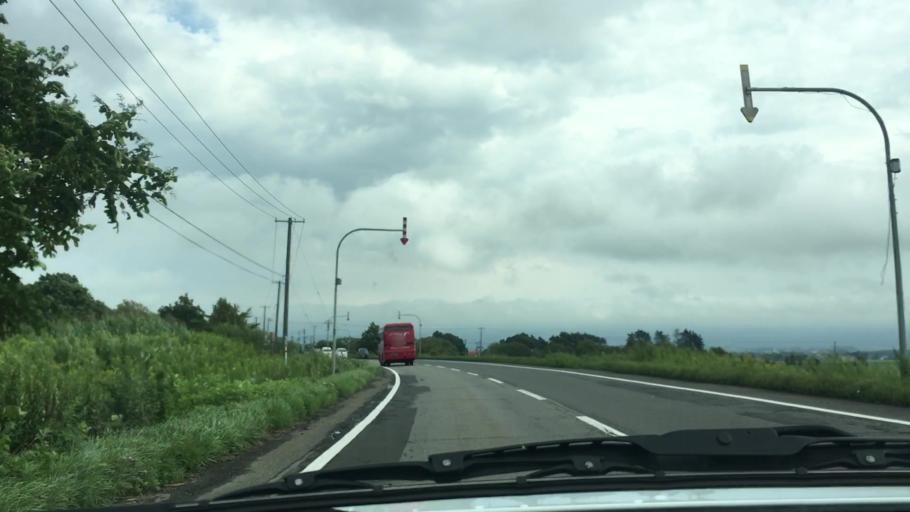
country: JP
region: Hokkaido
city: Chitose
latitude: 42.9431
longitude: 141.7621
